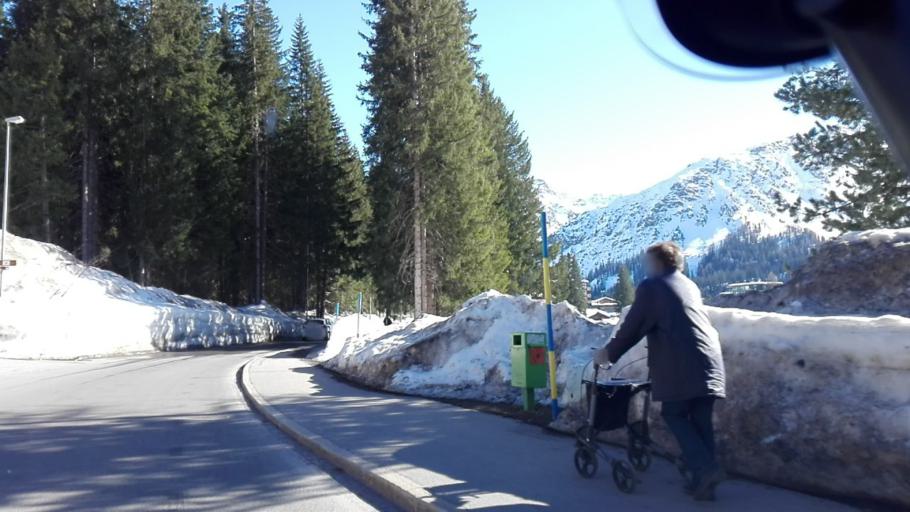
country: CH
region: Grisons
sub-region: Plessur District
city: Arosa
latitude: 46.7858
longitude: 9.6834
